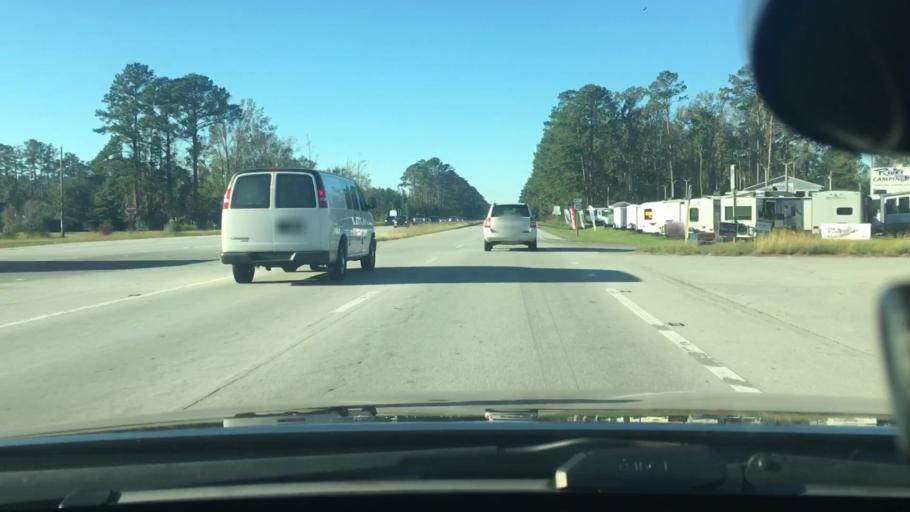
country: US
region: North Carolina
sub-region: Craven County
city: Fairfield Harbour
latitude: 35.0136
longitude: -76.9938
